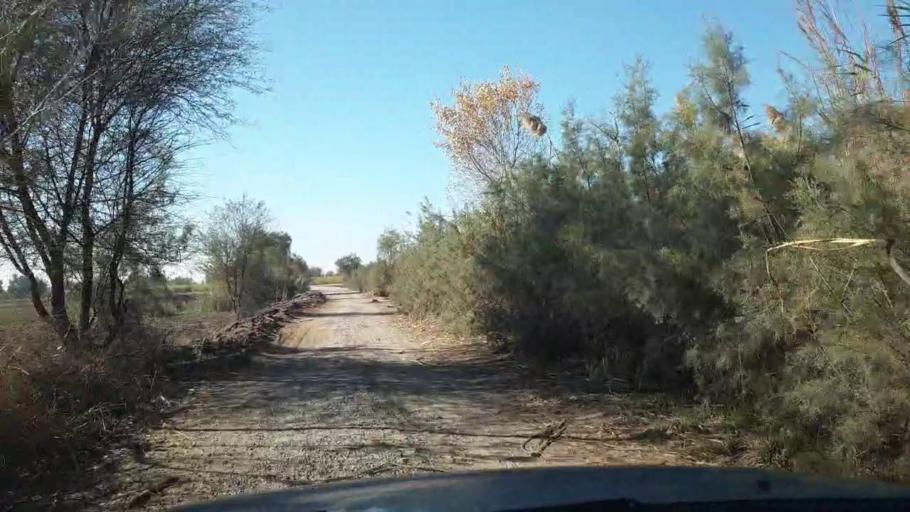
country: PK
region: Sindh
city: Ghotki
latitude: 28.0178
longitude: 69.2754
